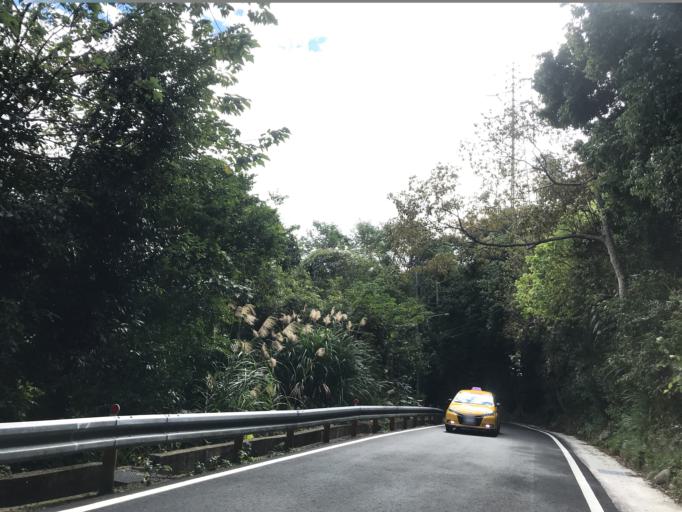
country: TW
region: Taiwan
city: Daxi
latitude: 24.8354
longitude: 121.2448
